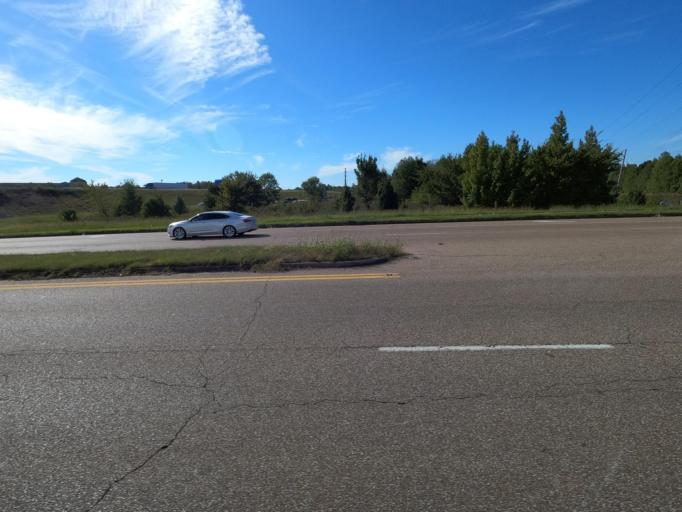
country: US
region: Tennessee
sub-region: Shelby County
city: Germantown
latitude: 35.0389
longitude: -89.7957
